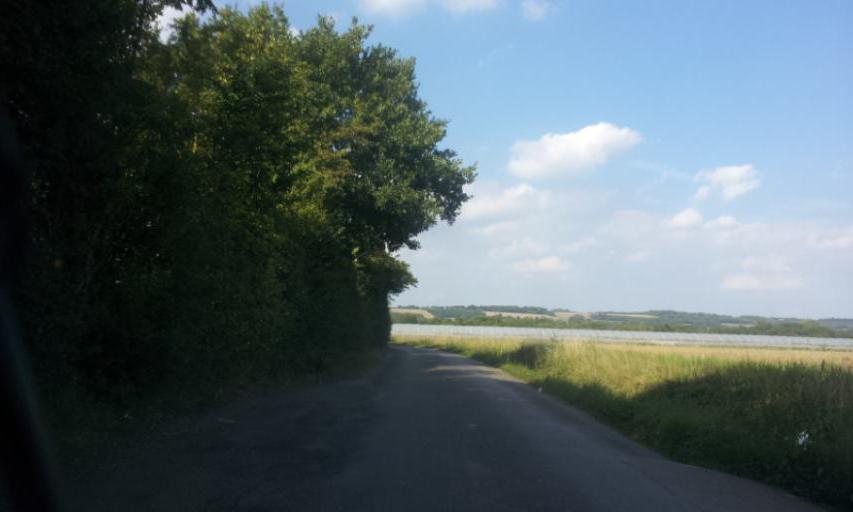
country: GB
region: England
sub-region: Kent
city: Yalding
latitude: 51.2152
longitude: 0.4367
